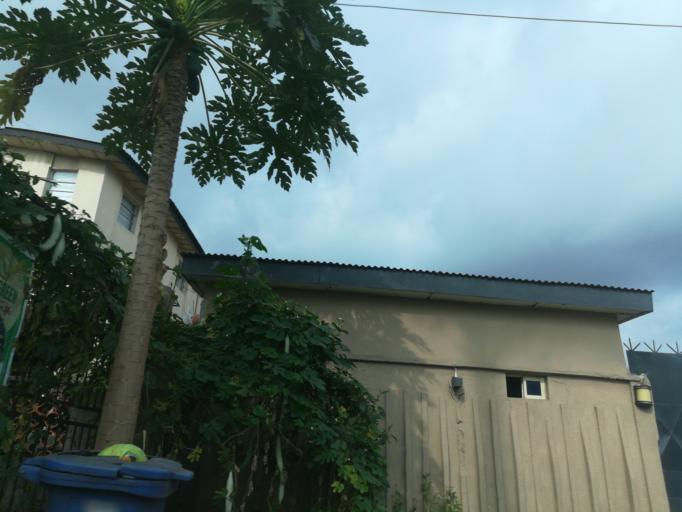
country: NG
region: Lagos
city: Oshodi
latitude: 6.5716
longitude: 3.3519
